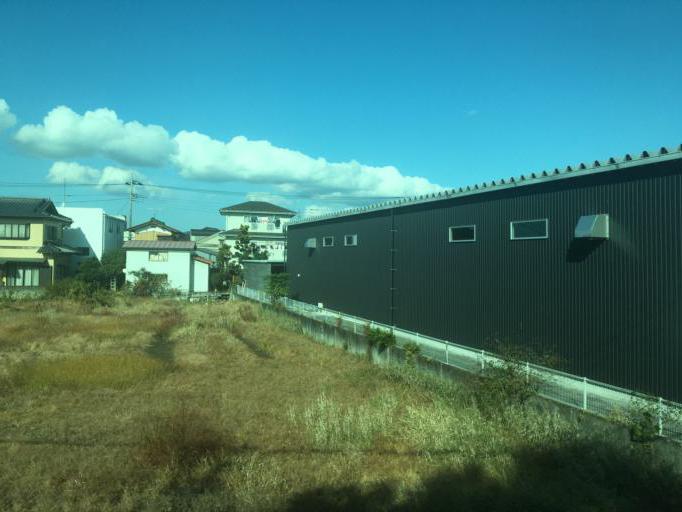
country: JP
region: Ibaraki
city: Kasama
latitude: 36.3723
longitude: 140.2496
